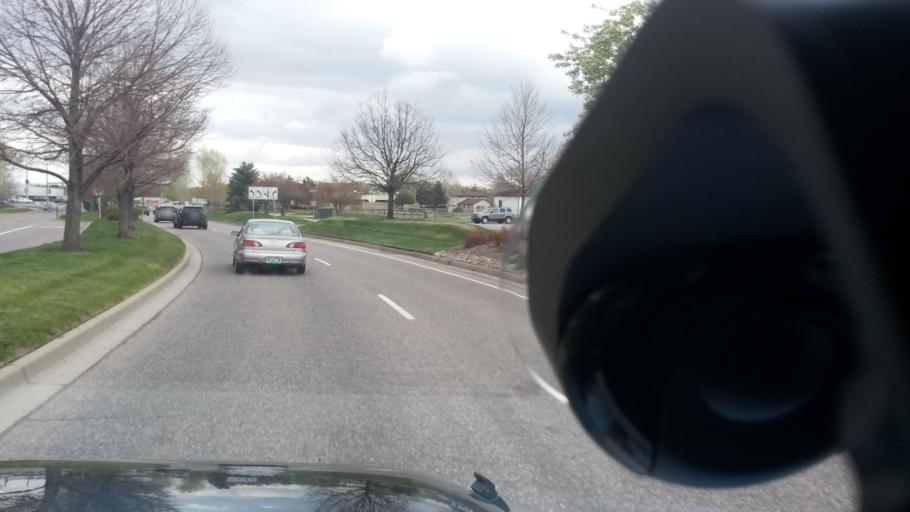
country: US
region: Colorado
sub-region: Boulder County
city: Superior
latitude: 39.9553
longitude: -105.1691
